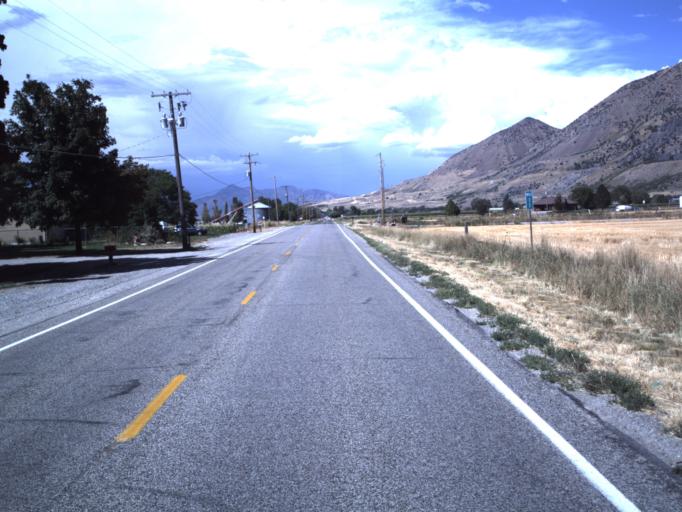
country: US
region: Utah
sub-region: Box Elder County
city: Honeyville
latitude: 41.6718
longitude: -112.0897
